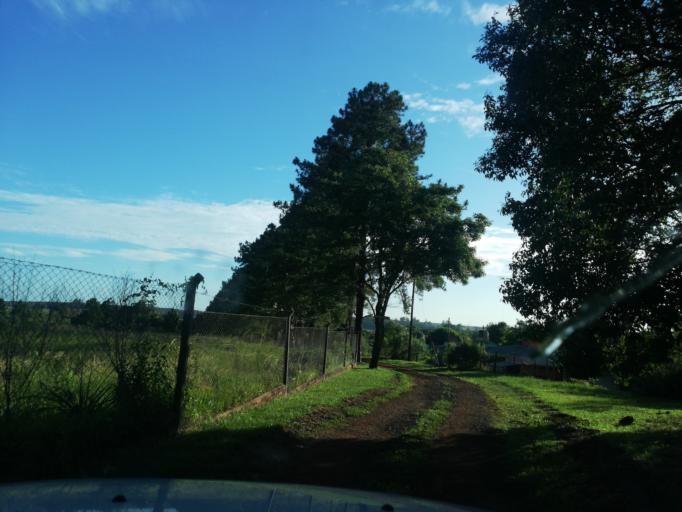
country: AR
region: Misiones
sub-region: Departamento de Capital
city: Posadas
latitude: -27.4289
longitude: -55.9226
